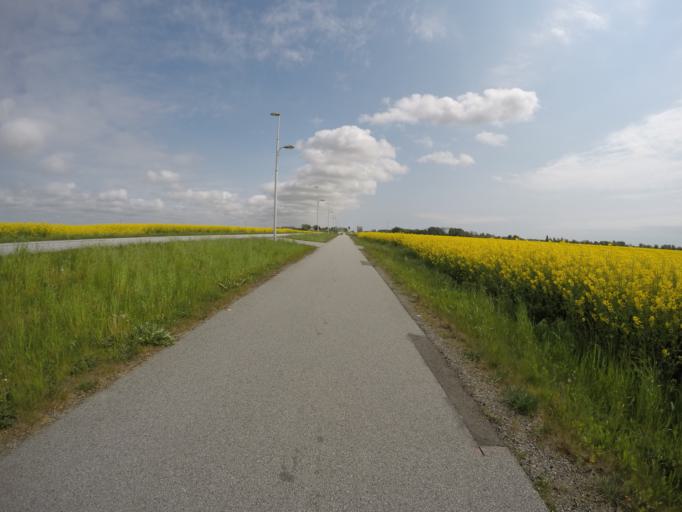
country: SE
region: Skane
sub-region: Malmo
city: Tygelsjo
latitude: 55.5362
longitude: 12.9864
